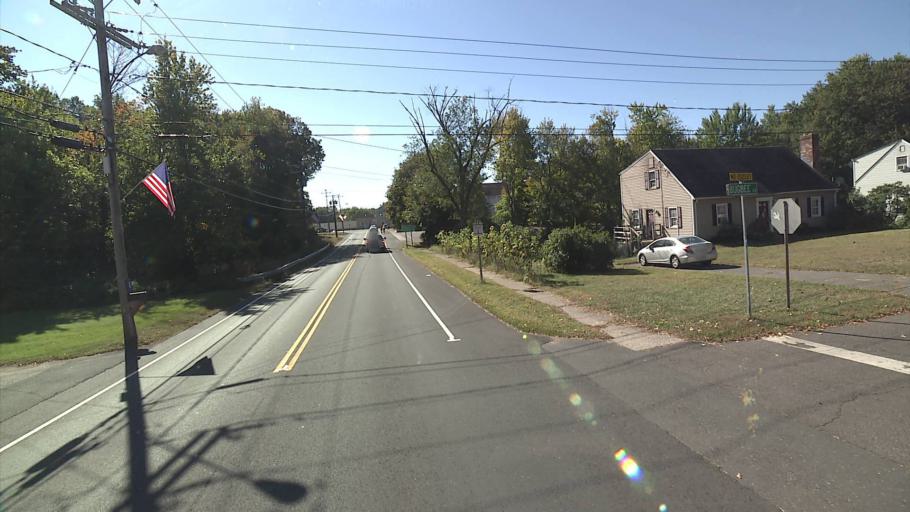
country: US
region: Connecticut
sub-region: Tolland County
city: Somers
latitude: 41.9870
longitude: -72.4474
